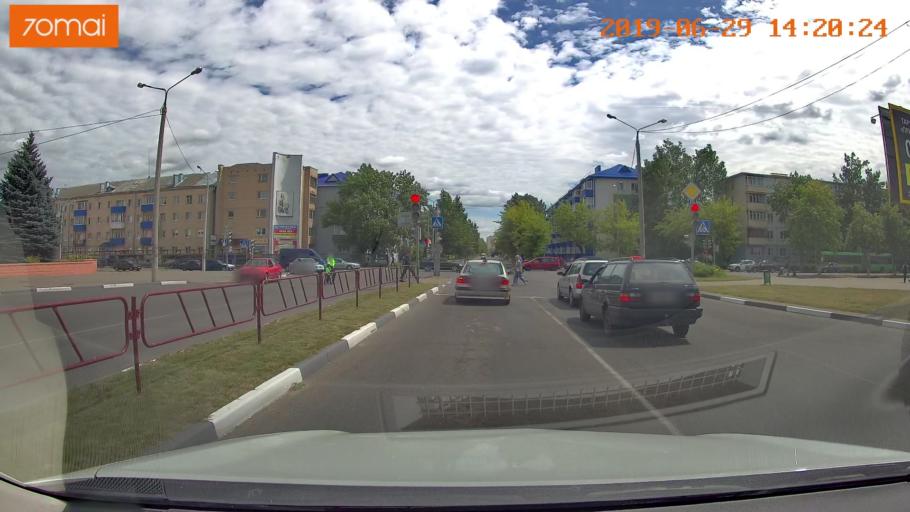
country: BY
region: Minsk
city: Salihorsk
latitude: 52.7926
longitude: 27.5431
